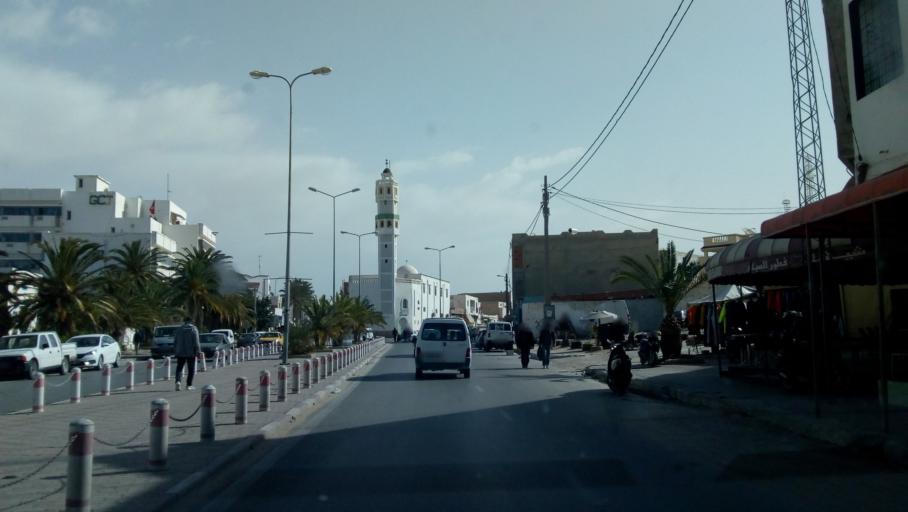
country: TN
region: Qabis
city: Gabes
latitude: 33.8844
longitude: 10.0878
